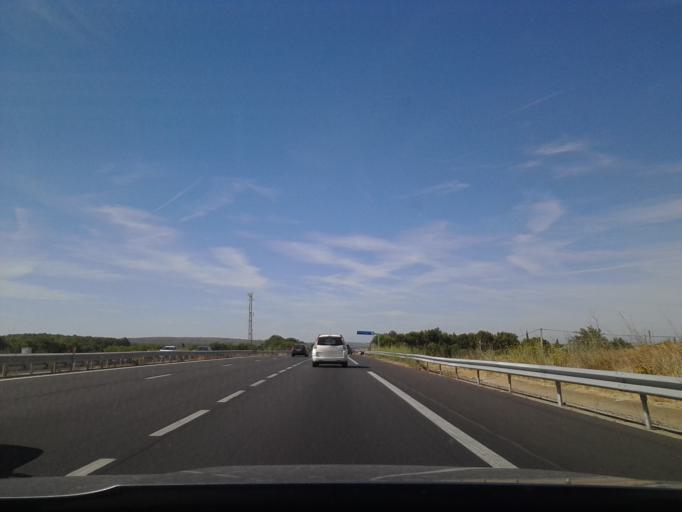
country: FR
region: Languedoc-Roussillon
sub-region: Departement de l'Herault
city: Lespignan
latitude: 43.2688
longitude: 3.1784
